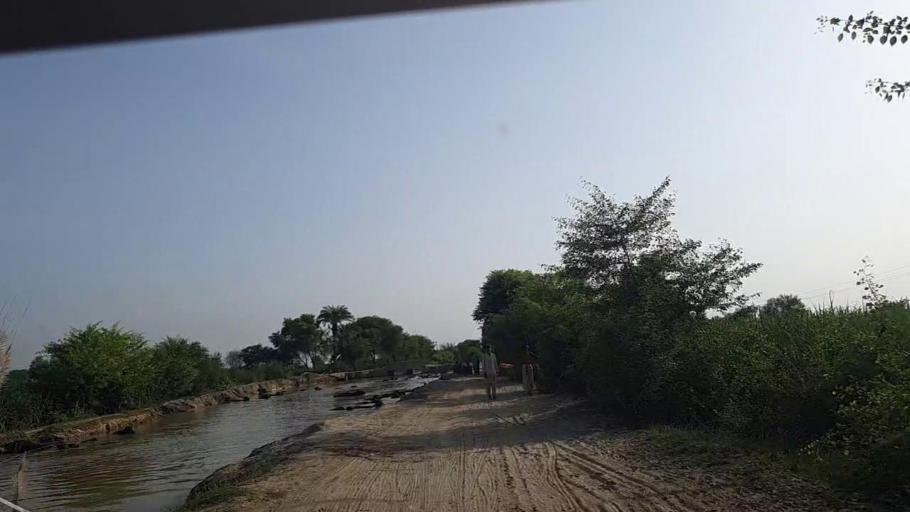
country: PK
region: Sindh
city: Ghotki
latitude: 27.9946
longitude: 69.2600
